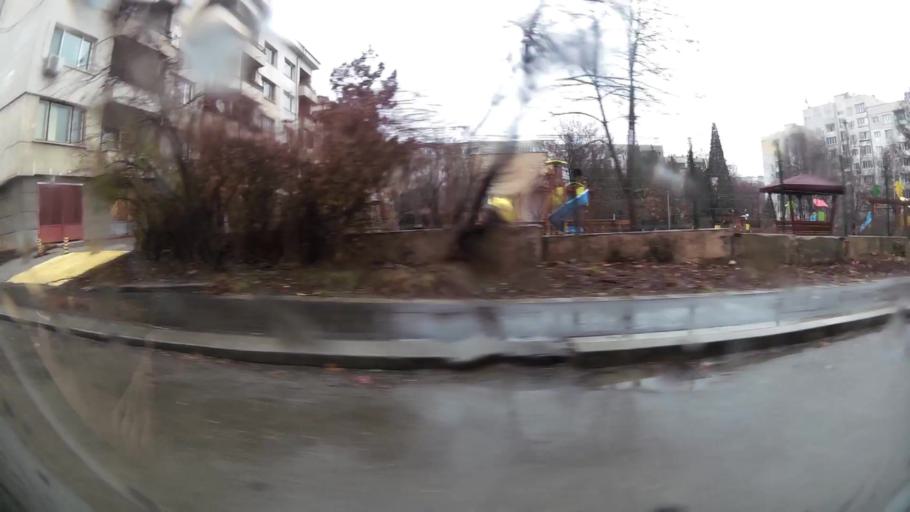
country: BG
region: Sofia-Capital
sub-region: Stolichna Obshtina
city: Sofia
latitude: 42.6555
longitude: 23.3623
